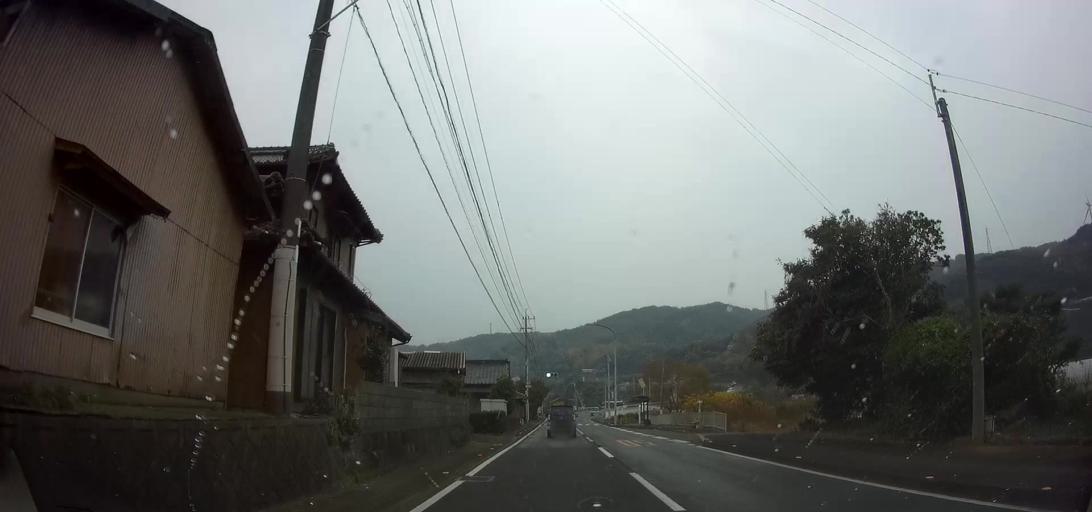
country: JP
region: Nagasaki
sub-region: Isahaya-shi
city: Isahaya
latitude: 32.7923
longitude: 130.1847
